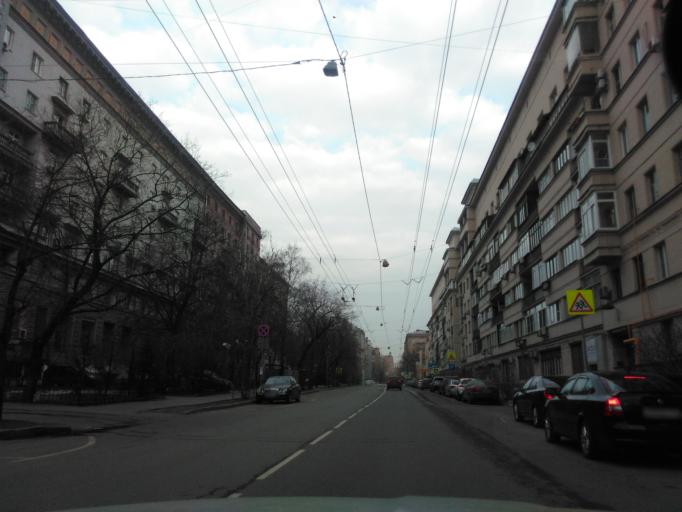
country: RU
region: Moscow
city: Moscow
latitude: 55.7729
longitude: 37.6020
